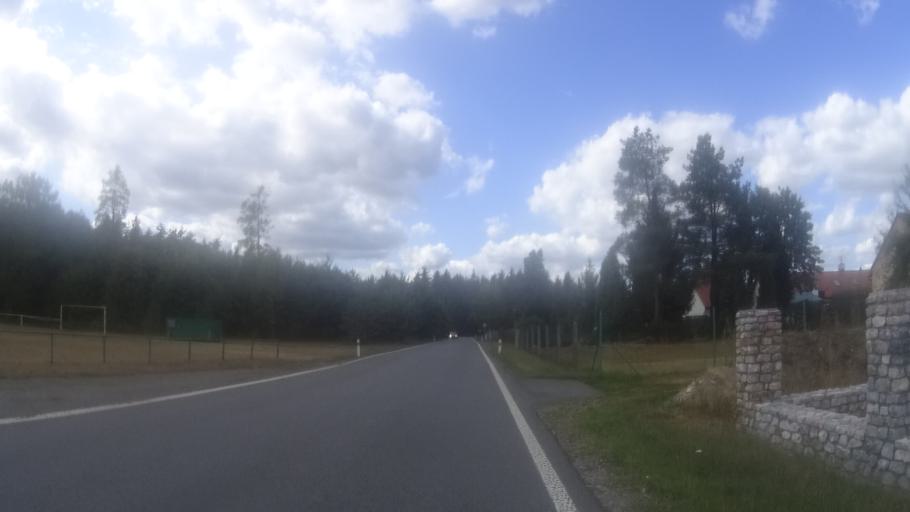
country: CZ
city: Borohradek
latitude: 50.0778
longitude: 16.1249
